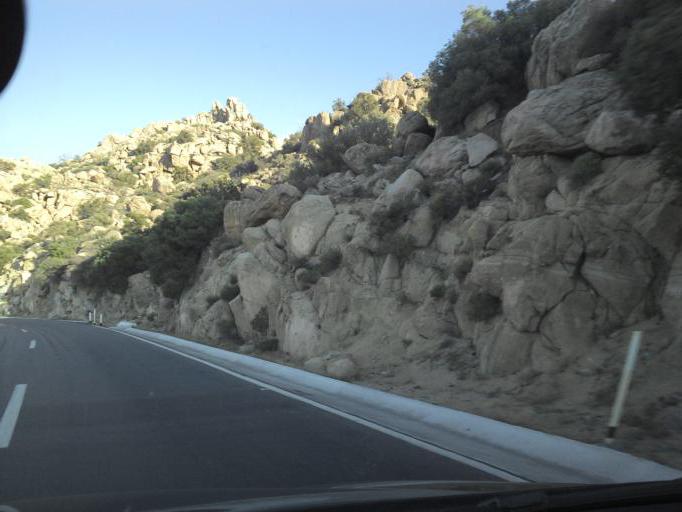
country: MX
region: Baja California
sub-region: Tecate
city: Cereso del Hongo
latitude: 32.5779
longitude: -116.0382
